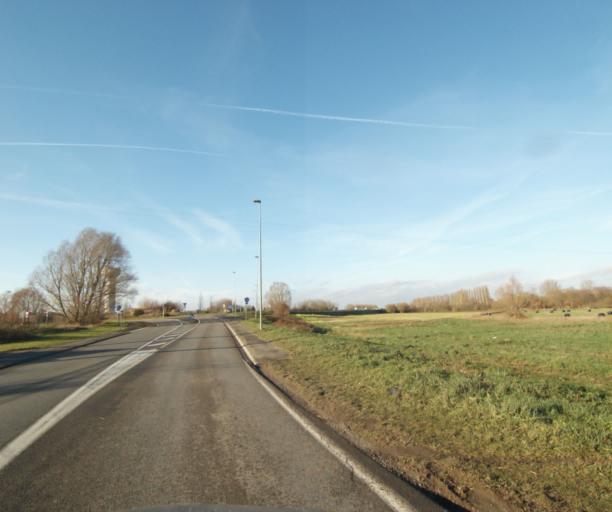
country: FR
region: Nord-Pas-de-Calais
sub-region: Departement du Nord
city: Curgies
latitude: 50.3336
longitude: 3.5915
